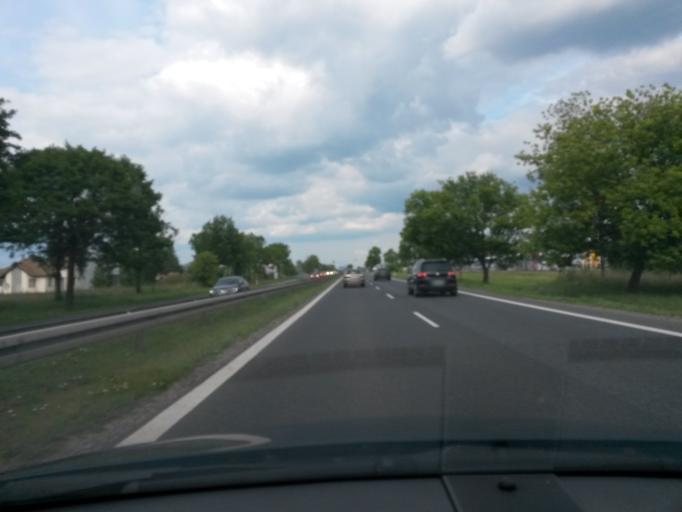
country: PL
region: Masovian Voivodeship
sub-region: Powiat pruszkowski
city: Nadarzyn
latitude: 52.0732
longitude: 20.7696
